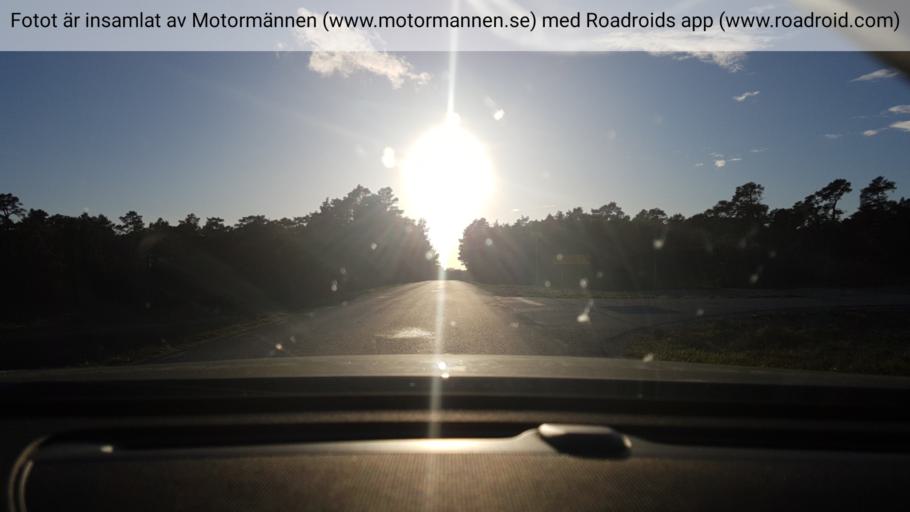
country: SE
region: Gotland
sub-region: Gotland
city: Slite
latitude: 57.8496
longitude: 18.6747
